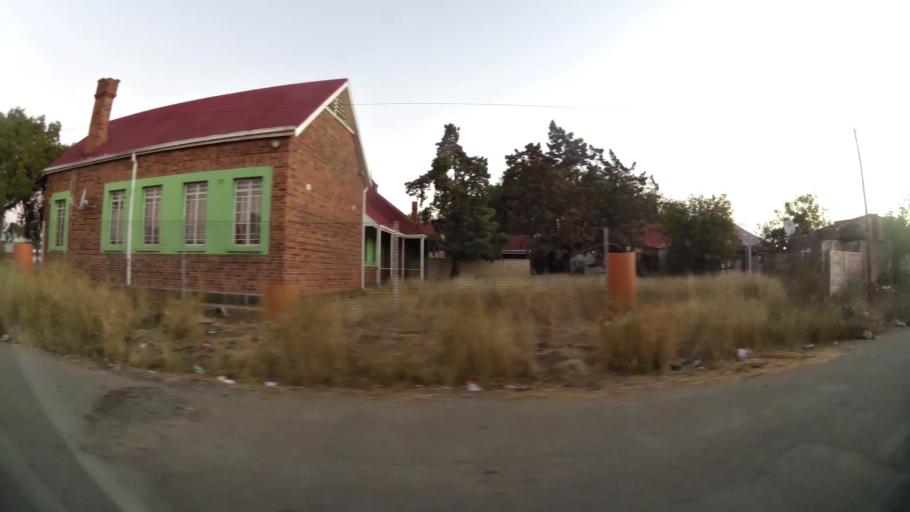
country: ZA
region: Northern Cape
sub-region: Frances Baard District Municipality
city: Kimberley
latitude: -28.7267
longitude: 24.7669
